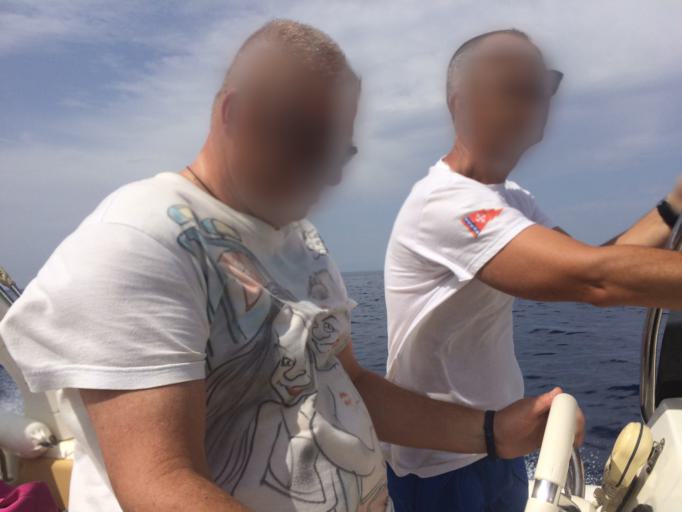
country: IT
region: Tuscany
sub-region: Provincia di Livorno
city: Capraia Isola
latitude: 43.0475
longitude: 9.7933
